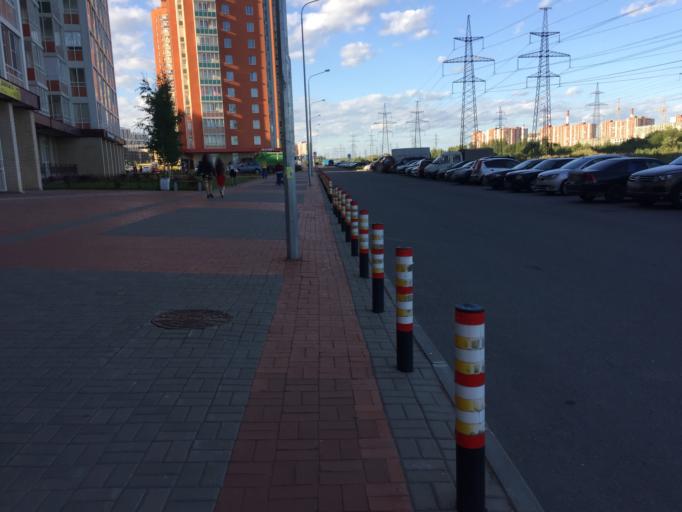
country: RU
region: Leningrad
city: Murino
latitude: 60.0572
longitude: 30.4427
